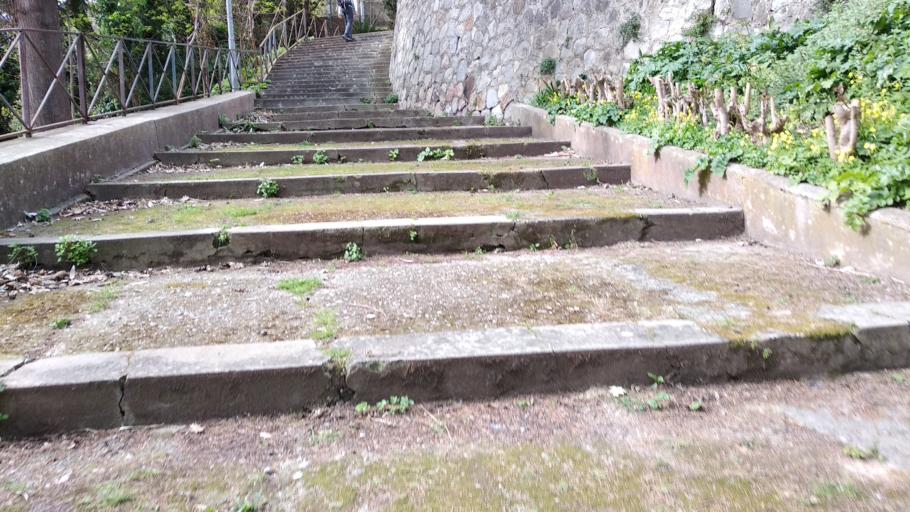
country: IT
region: Sicily
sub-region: Messina
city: Villafranca Tirrena
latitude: 38.2212
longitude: 15.4534
